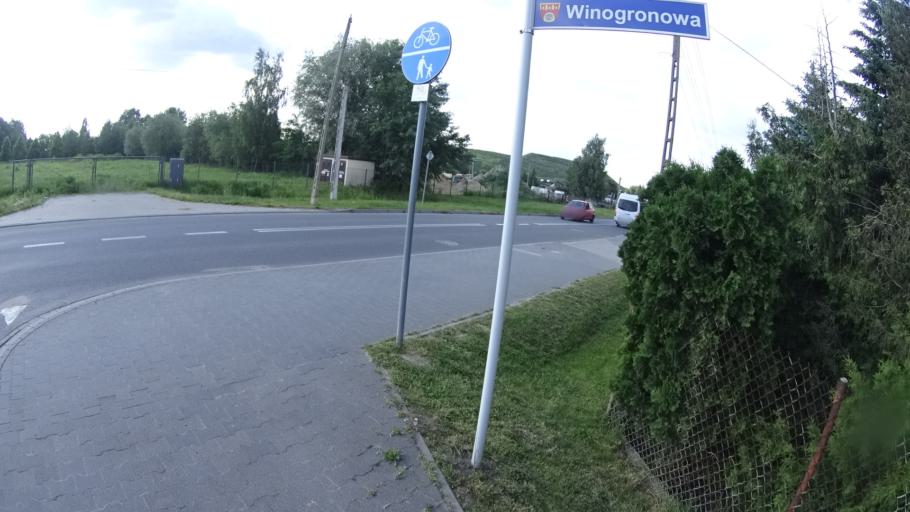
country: PL
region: Masovian Voivodeship
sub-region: Powiat pruszkowski
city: Pruszkow
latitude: 52.1721
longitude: 20.7768
